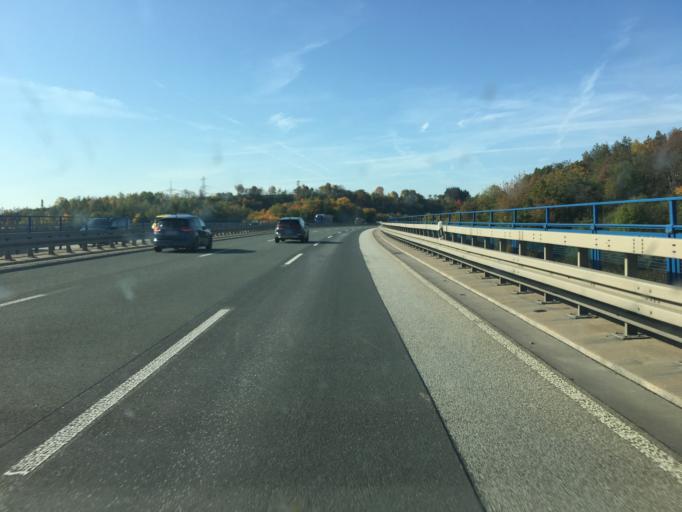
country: DE
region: Hesse
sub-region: Regierungsbezirk Giessen
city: Asslar
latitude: 50.5962
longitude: 8.4895
